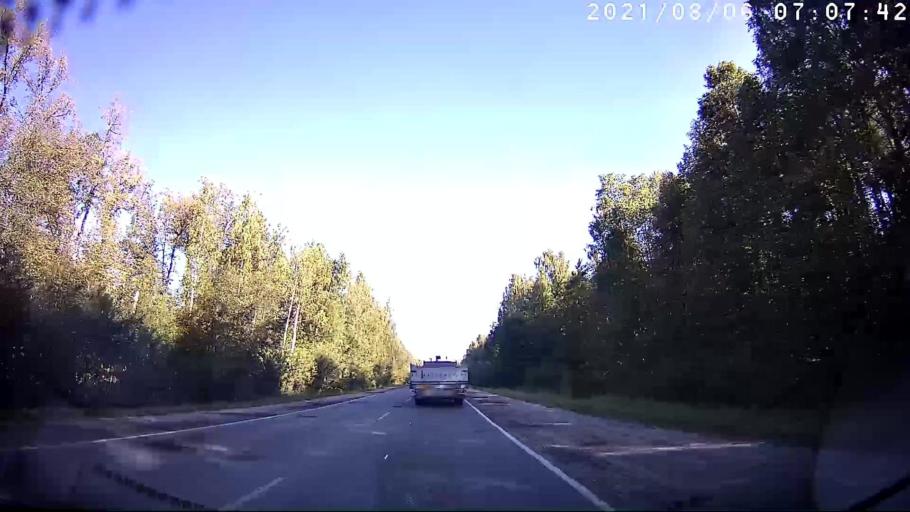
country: RU
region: Mariy-El
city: Yoshkar-Ola
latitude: 56.5649
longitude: 47.9771
